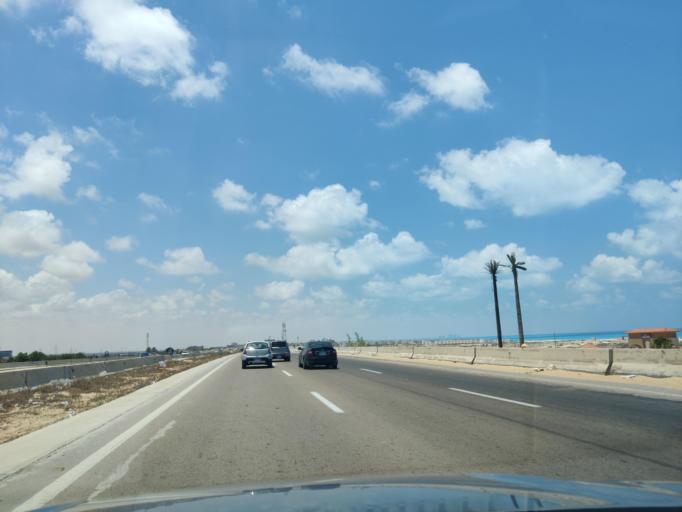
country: EG
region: Muhafazat Matruh
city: Al `Alamayn
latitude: 30.8287
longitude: 29.2087
